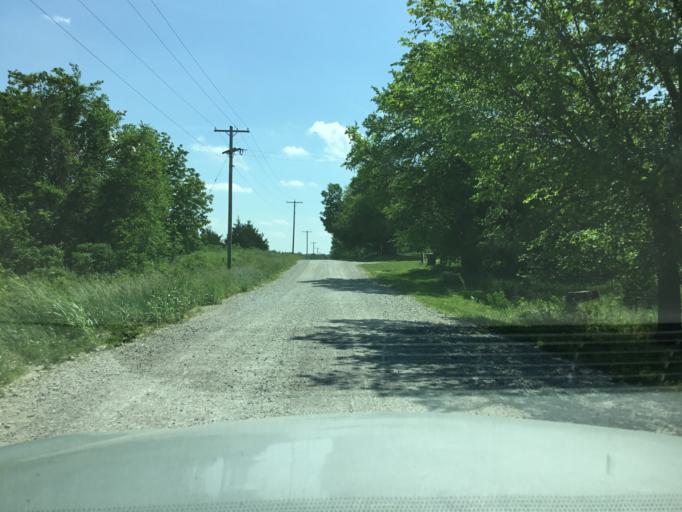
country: US
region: Kansas
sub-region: Labette County
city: Parsons
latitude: 37.3110
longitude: -95.2571
